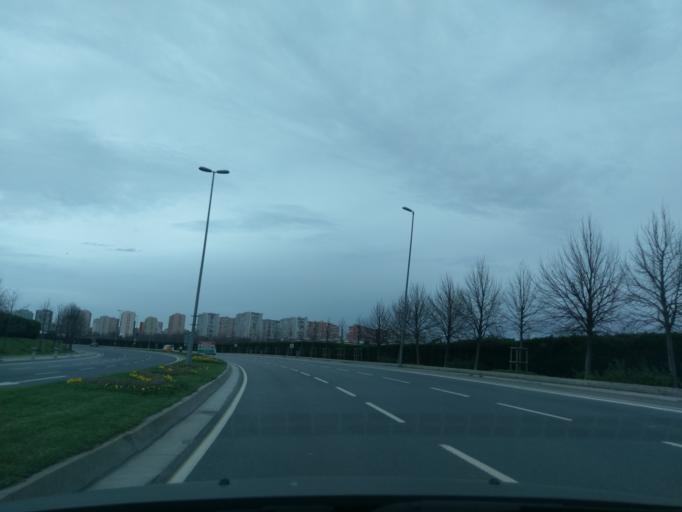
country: TR
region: Istanbul
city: Bahcelievler
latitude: 40.9787
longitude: 28.8407
